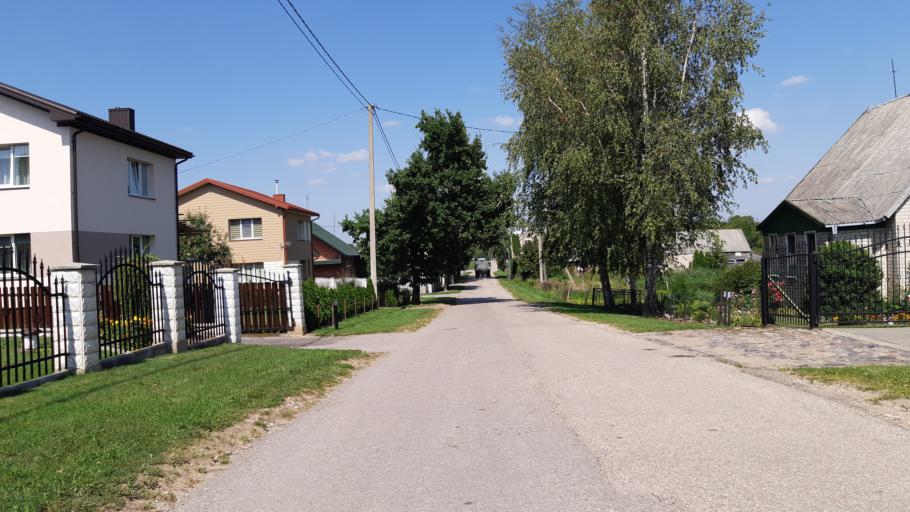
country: LT
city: Virbalis
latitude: 54.6221
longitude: 22.8173
